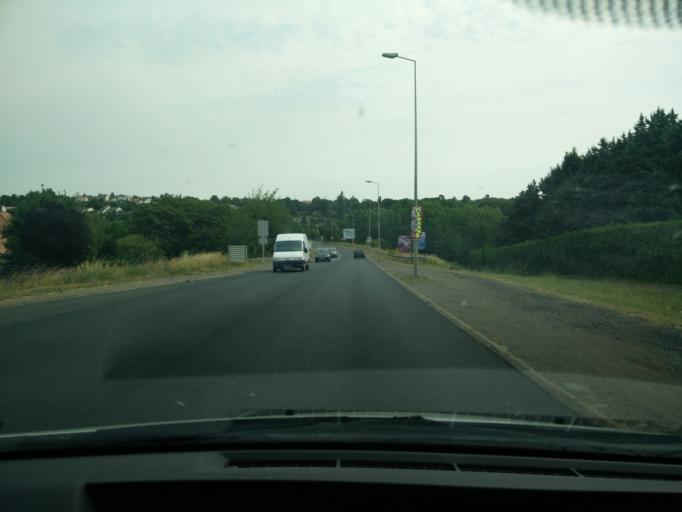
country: FR
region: Poitou-Charentes
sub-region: Departement des Deux-Sevres
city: Saint-Jean-de-Thouars
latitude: 46.9710
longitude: -0.2072
